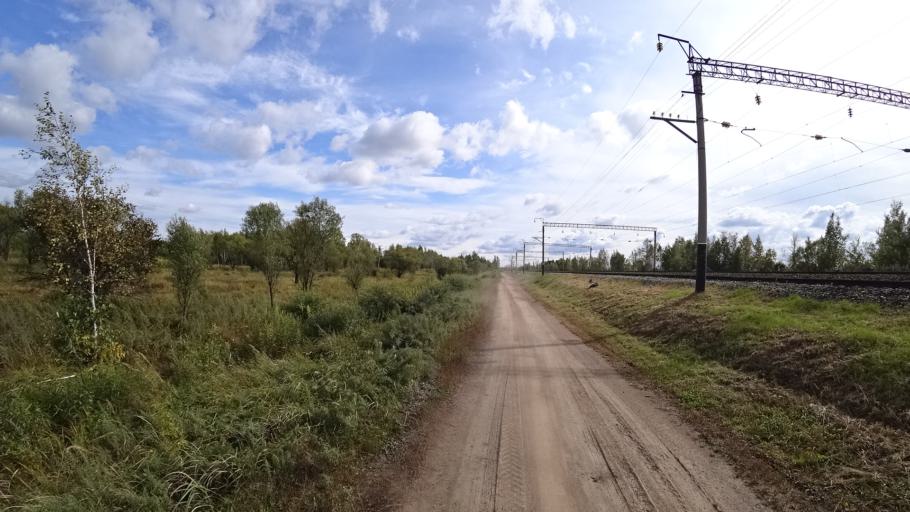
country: RU
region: Amur
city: Arkhara
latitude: 49.3466
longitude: 130.1630
